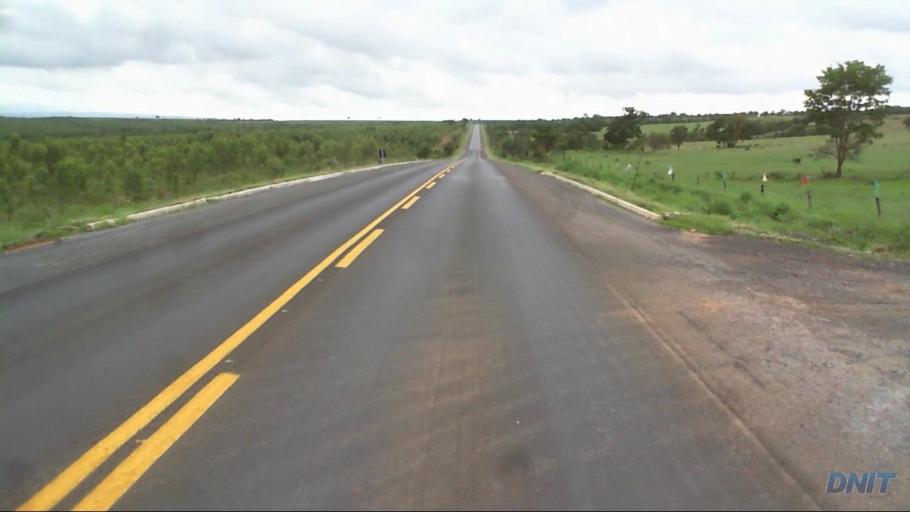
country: BR
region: Goias
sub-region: Barro Alto
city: Barro Alto
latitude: -15.2135
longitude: -48.6617
